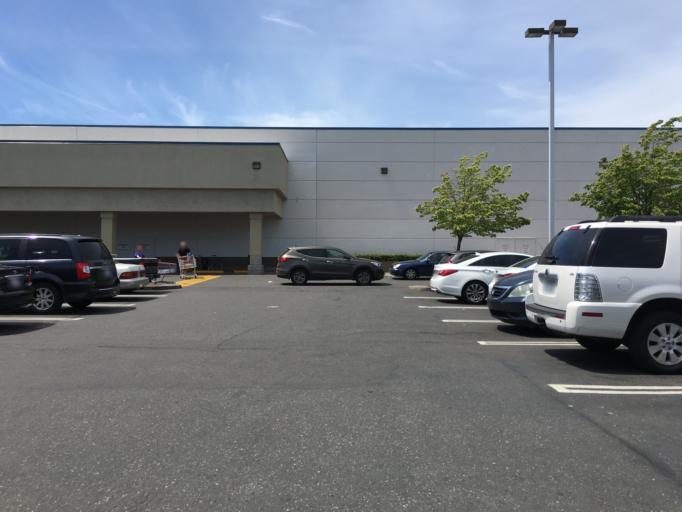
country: US
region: Washington
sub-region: Whatcom County
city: Bellingham
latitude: 48.7984
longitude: -122.4881
